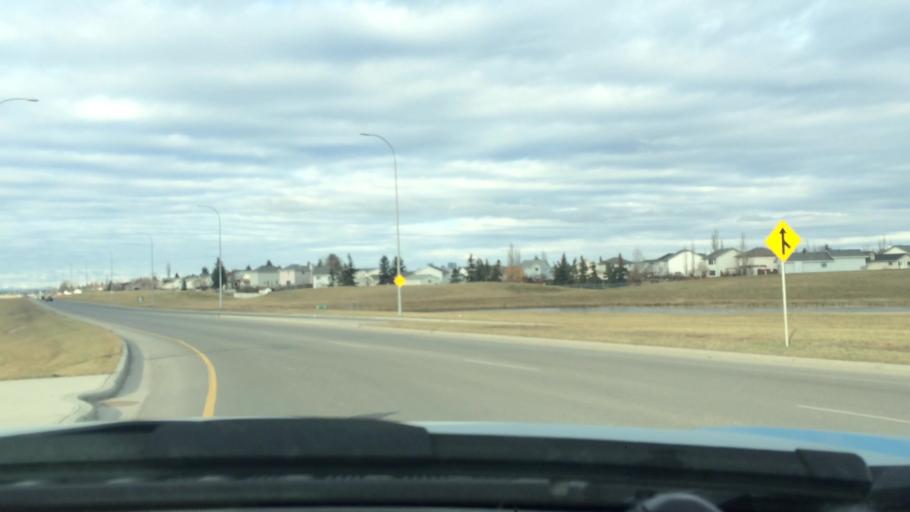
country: CA
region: Alberta
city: Calgary
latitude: 51.0149
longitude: -113.9587
